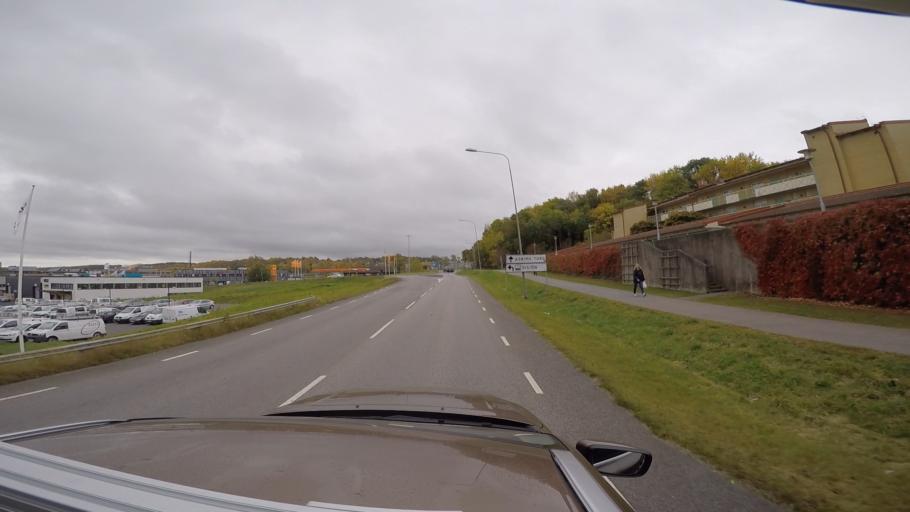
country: SE
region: Vaestra Goetaland
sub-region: Goteborg
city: Majorna
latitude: 57.6423
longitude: 11.9404
